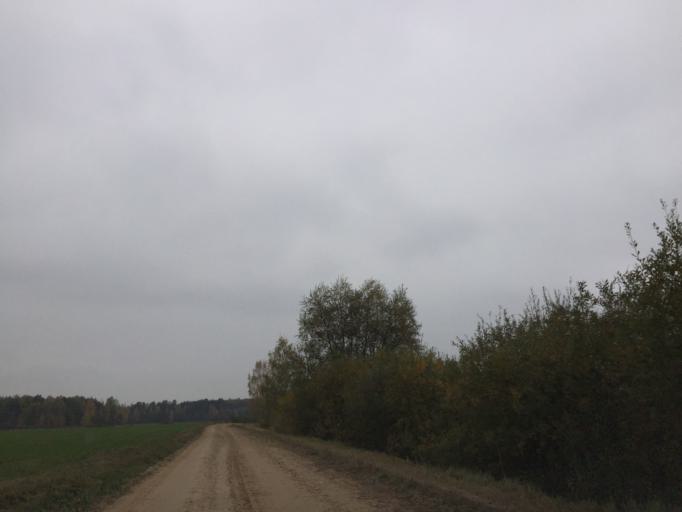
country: LV
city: Tireli
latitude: 56.6742
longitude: 23.4862
